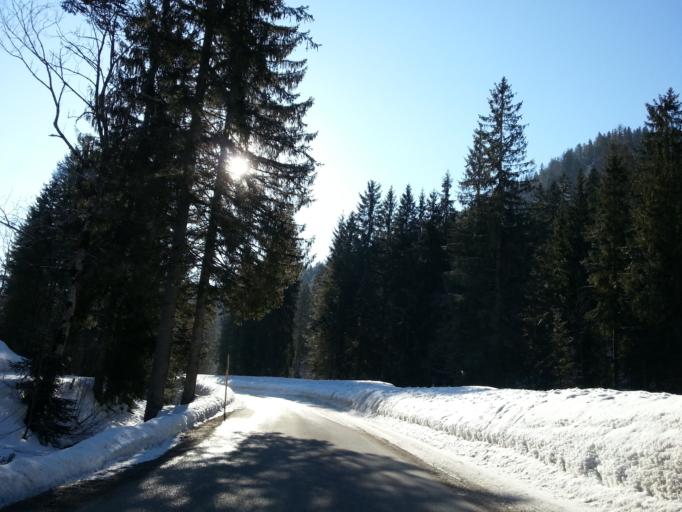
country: AT
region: Salzburg
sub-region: Politischer Bezirk Hallein
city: Abtenau
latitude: 47.4974
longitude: 13.3819
